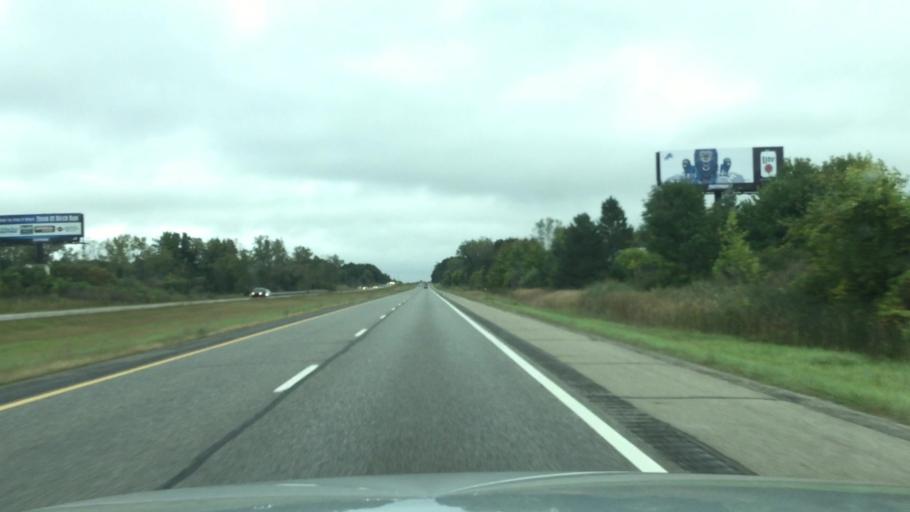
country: US
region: Michigan
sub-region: Genesee County
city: Flint
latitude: 42.9425
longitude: -83.7112
